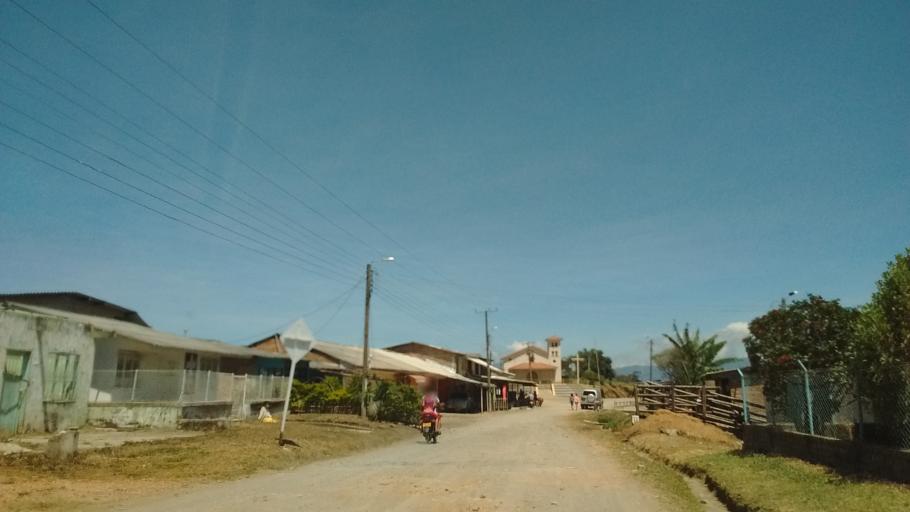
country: CO
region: Cauca
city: Lopez
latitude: 2.3960
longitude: -76.7477
